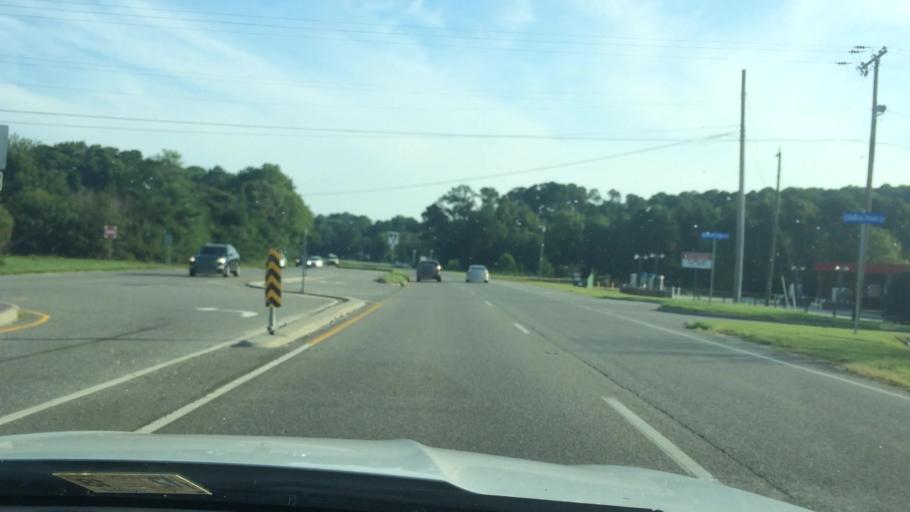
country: US
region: Virginia
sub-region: Gloucester County
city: Gloucester Point
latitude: 37.2610
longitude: -76.4941
